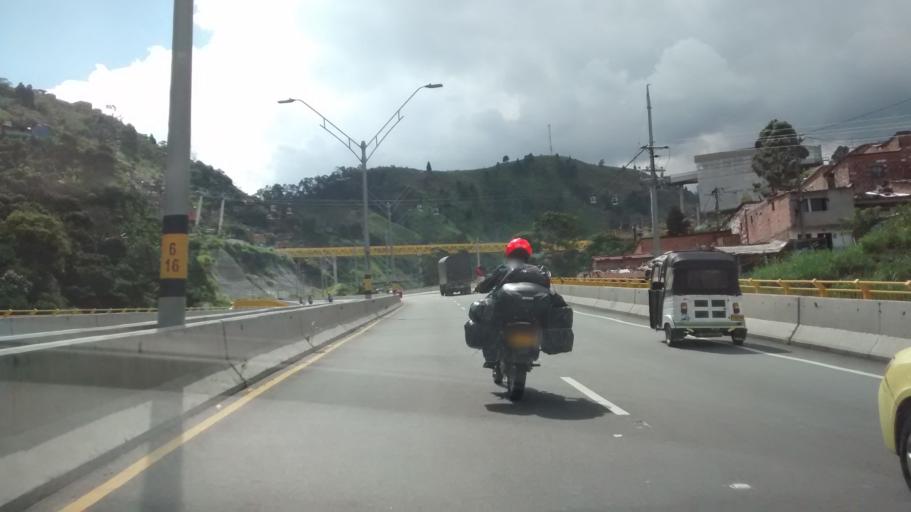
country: CO
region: Antioquia
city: Medellin
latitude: 6.2758
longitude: -75.6113
